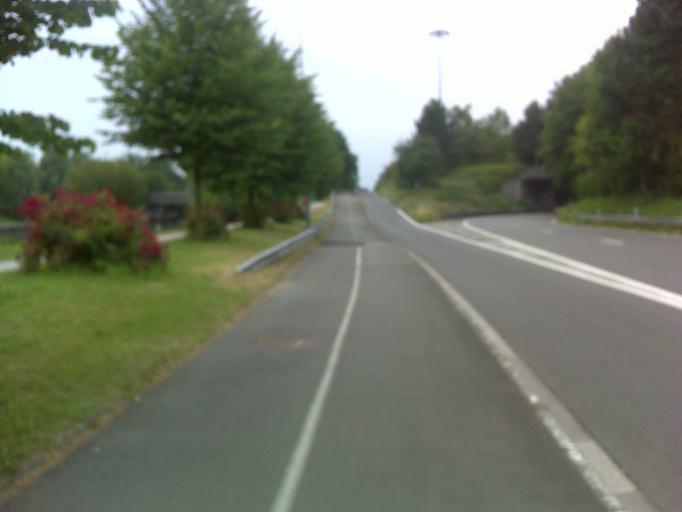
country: FR
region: Nord-Pas-de-Calais
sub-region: Departement du Nord
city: Saint-Andre-lez-Lille
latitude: 50.6506
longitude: 3.0495
